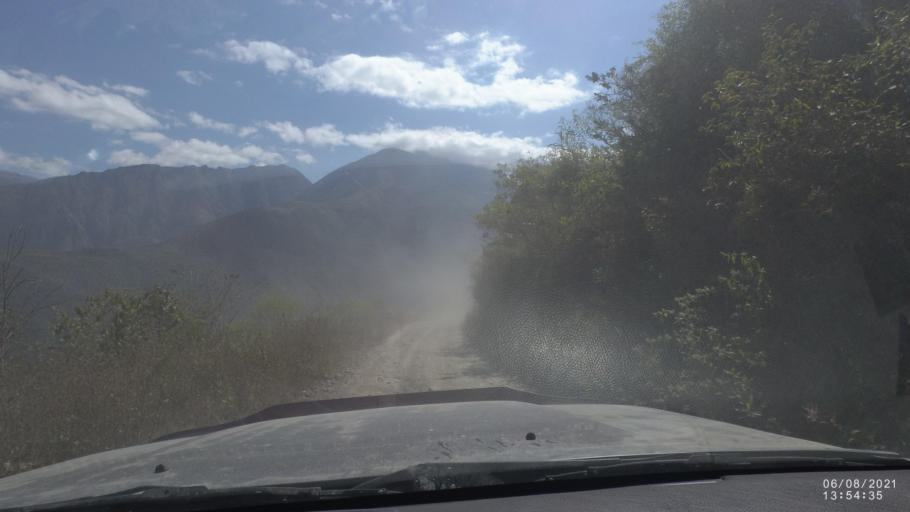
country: BO
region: La Paz
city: Quime
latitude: -16.6499
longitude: -66.7311
